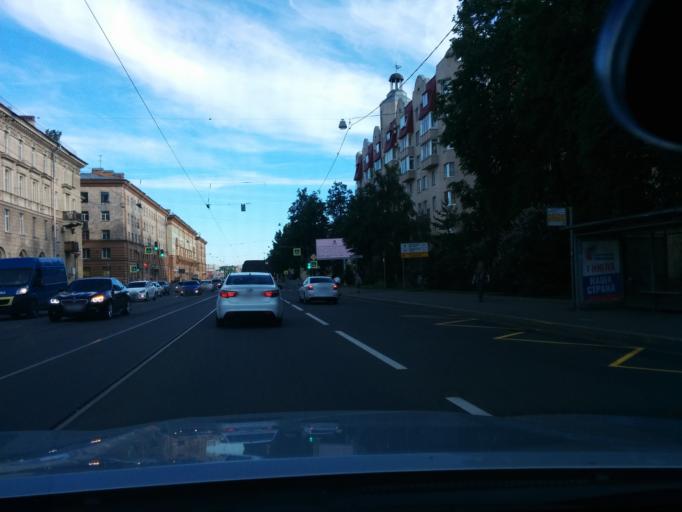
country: RU
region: Leningrad
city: Udel'naya
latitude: 60.0137
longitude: 30.3235
